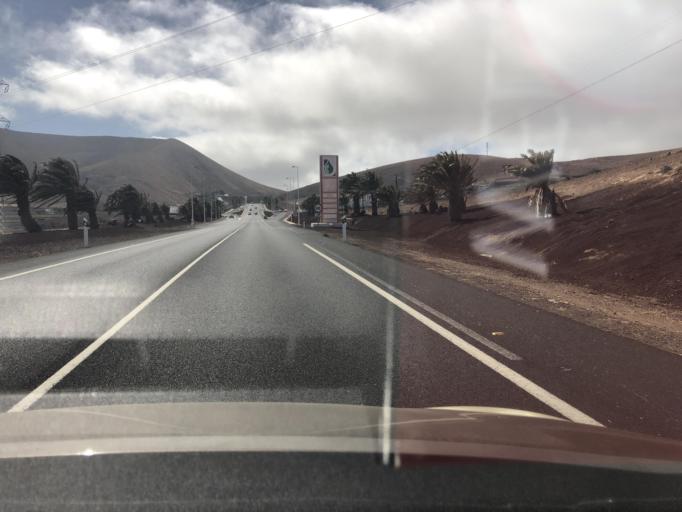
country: ES
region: Canary Islands
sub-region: Provincia de Las Palmas
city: Yaiza
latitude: 28.9375
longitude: -13.7333
